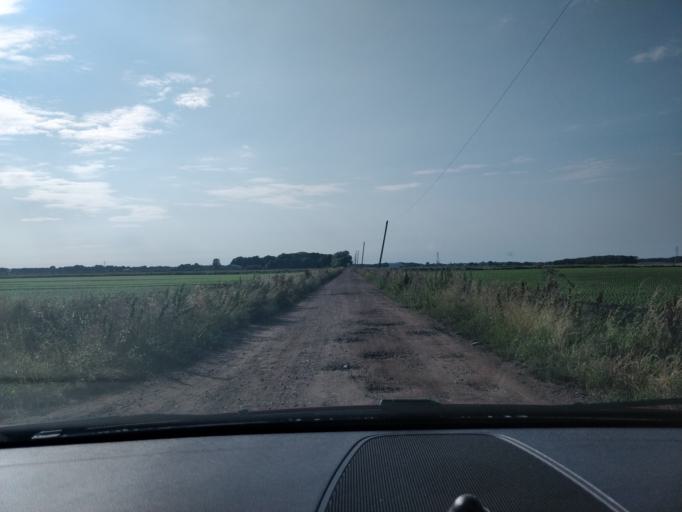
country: GB
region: England
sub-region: Lancashire
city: Banks
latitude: 53.6517
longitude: -2.9156
